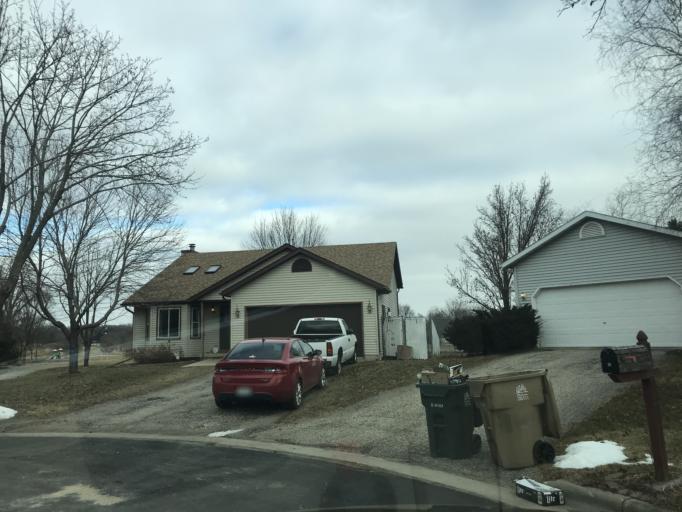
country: US
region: Wisconsin
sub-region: Dane County
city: Monona
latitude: 43.1093
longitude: -89.3005
